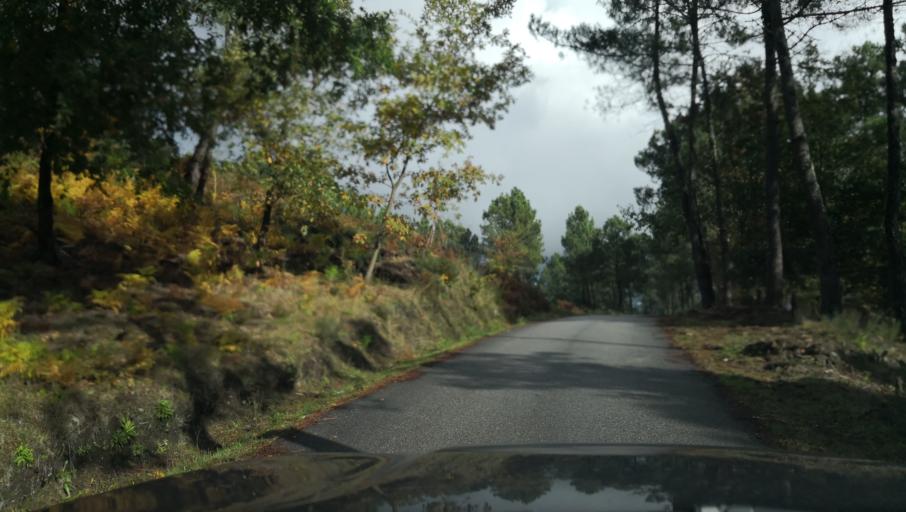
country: PT
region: Vila Real
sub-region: Vila Real
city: Vila Real
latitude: 41.3255
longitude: -7.7564
